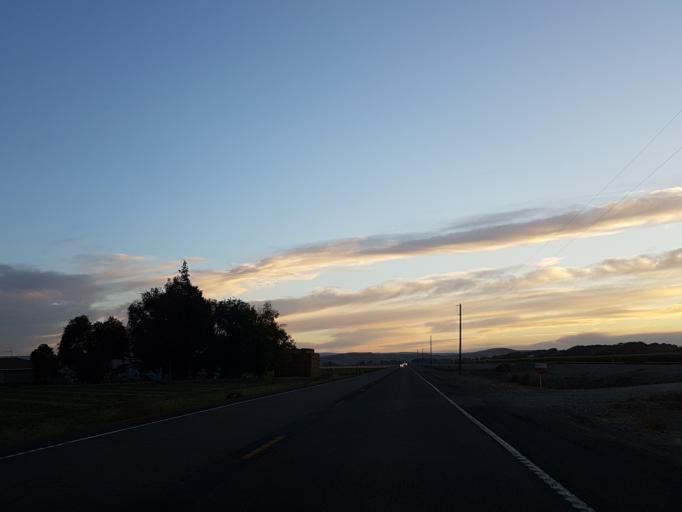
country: US
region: Oregon
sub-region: Malheur County
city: Vale
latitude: 43.9599
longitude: -117.2819
